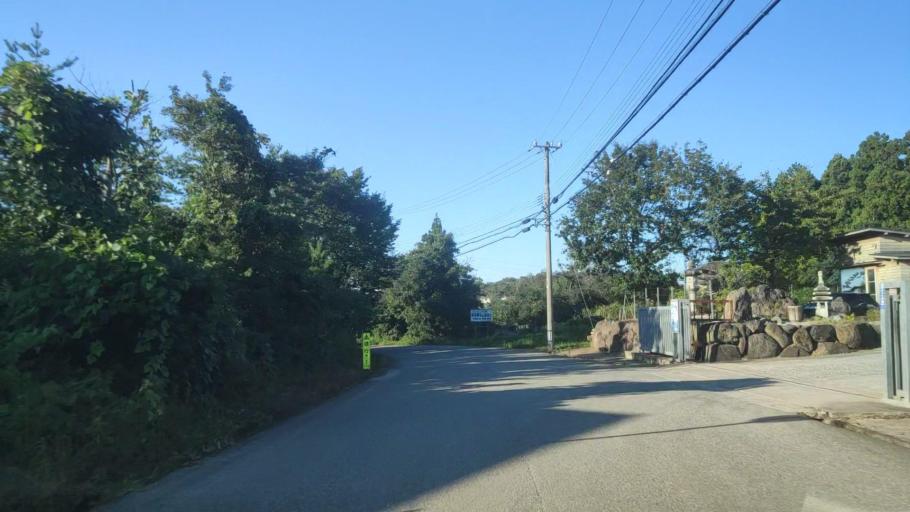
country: JP
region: Ishikawa
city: Nanao
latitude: 37.1287
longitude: 136.9317
